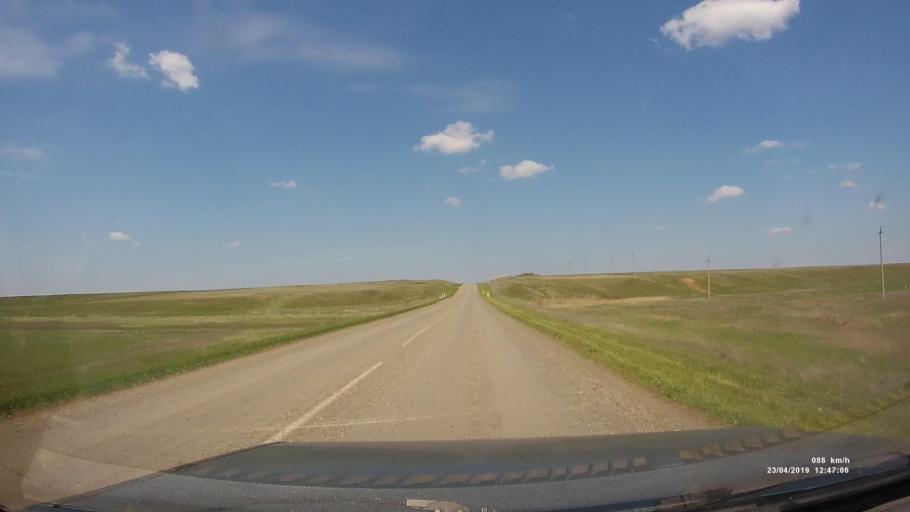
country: RU
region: Kalmykiya
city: Yashalta
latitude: 46.5079
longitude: 42.6385
